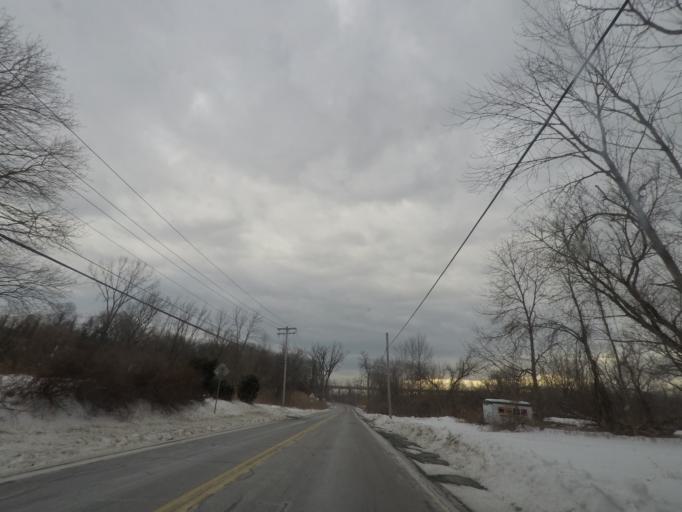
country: US
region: New York
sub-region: Rensselaer County
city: Castleton-on-Hudson
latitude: 42.5156
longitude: -73.7624
